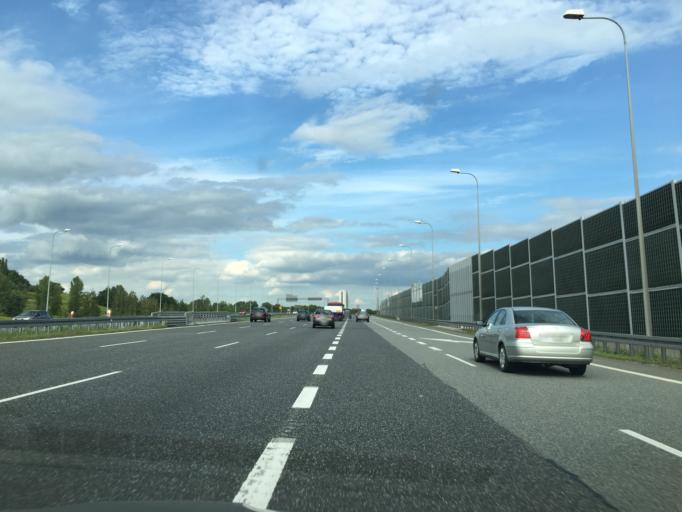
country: PL
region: Silesian Voivodeship
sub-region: Powiat gliwicki
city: Przyszowice
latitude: 50.2674
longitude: 18.7491
